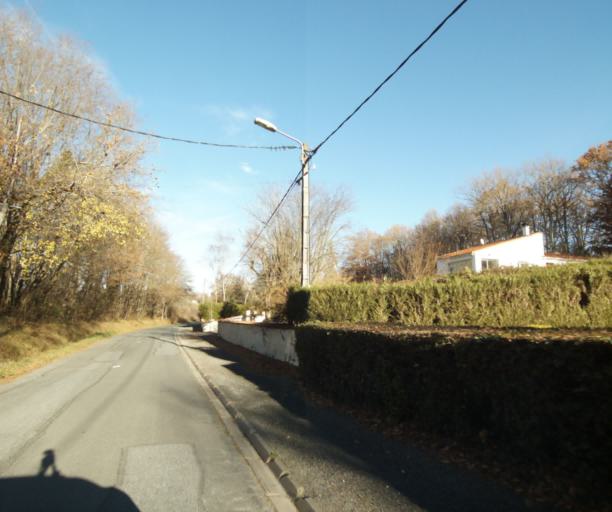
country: FR
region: Poitou-Charentes
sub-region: Departement de la Charente-Maritime
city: Fontcouverte
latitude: 45.7521
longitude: -0.5651
